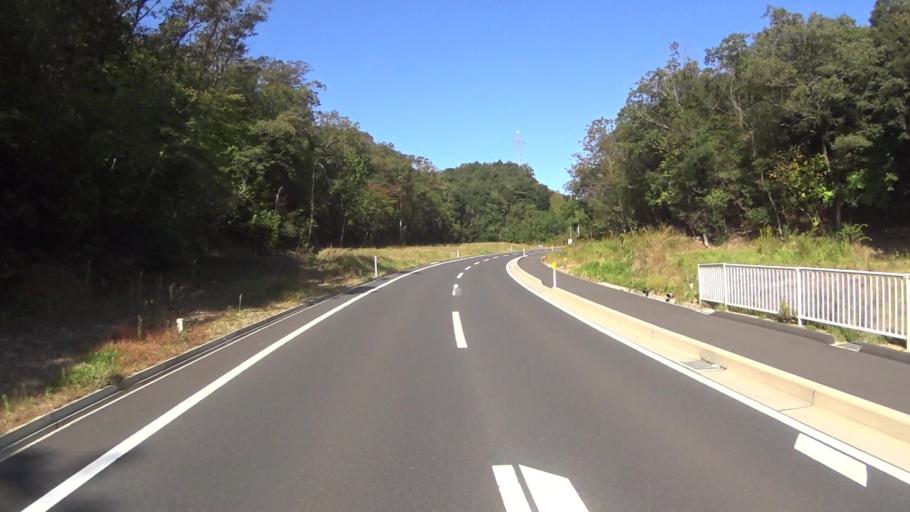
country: JP
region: Kyoto
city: Miyazu
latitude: 35.6727
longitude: 135.0750
